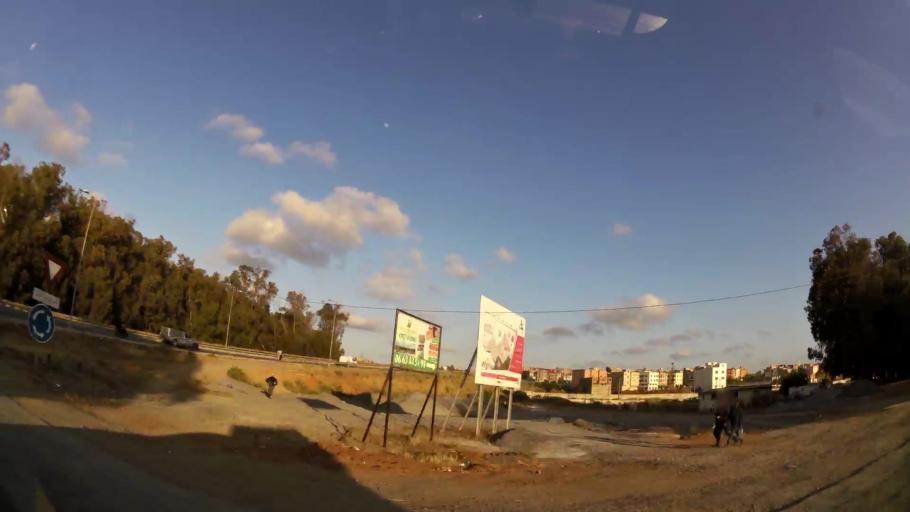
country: MA
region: Rabat-Sale-Zemmour-Zaer
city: Sale
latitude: 34.1300
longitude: -6.7333
